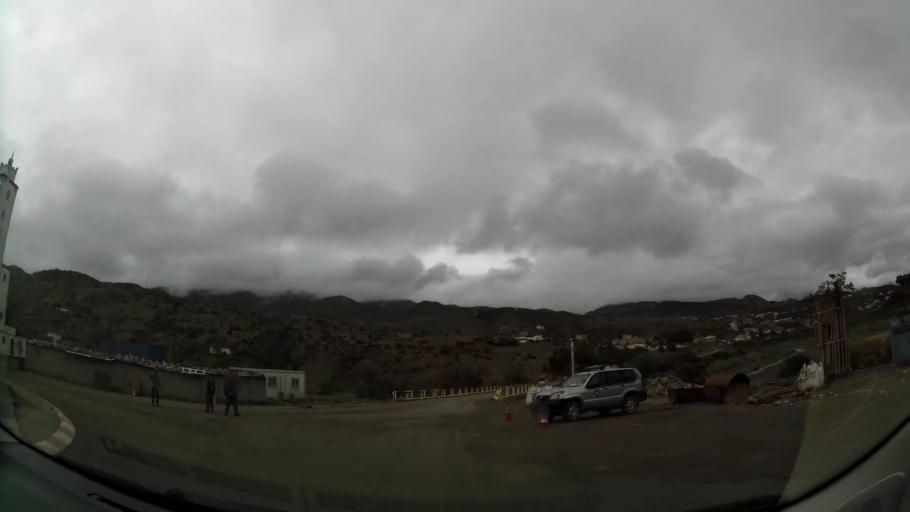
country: MA
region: Taza-Al Hoceima-Taounate
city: Imzourene
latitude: 34.9653
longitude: -3.8138
